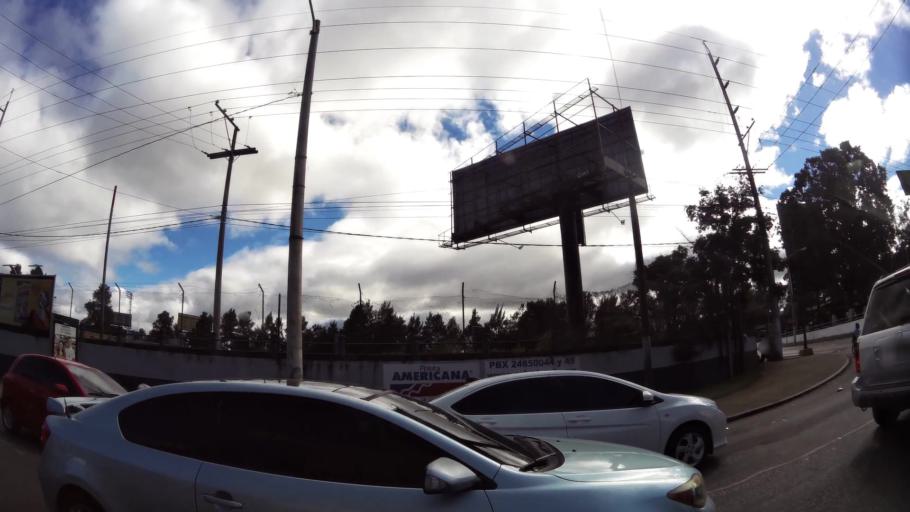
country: GT
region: Guatemala
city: Guatemala City
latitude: 14.6136
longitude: -90.5106
